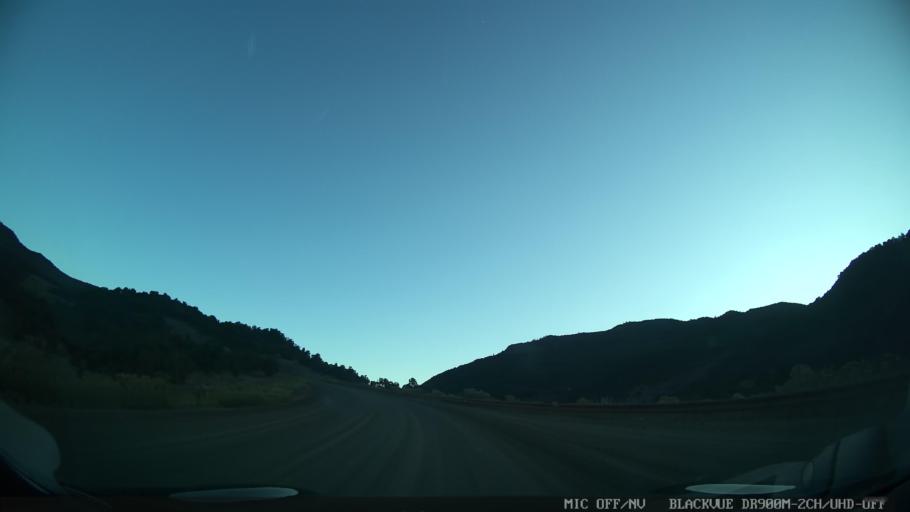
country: US
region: Colorado
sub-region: Eagle County
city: Edwards
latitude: 39.8564
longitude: -106.6443
